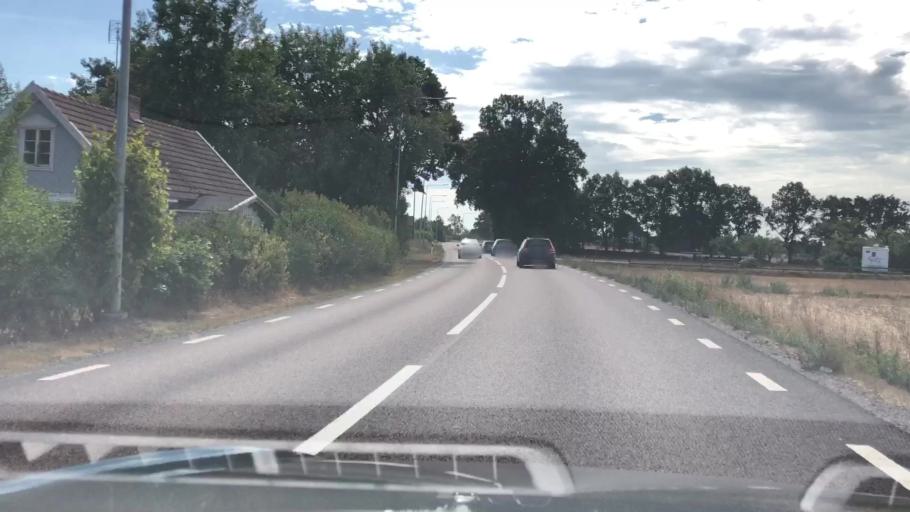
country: SE
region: Kalmar
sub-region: Torsas Kommun
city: Torsas
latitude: 56.3816
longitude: 16.0691
